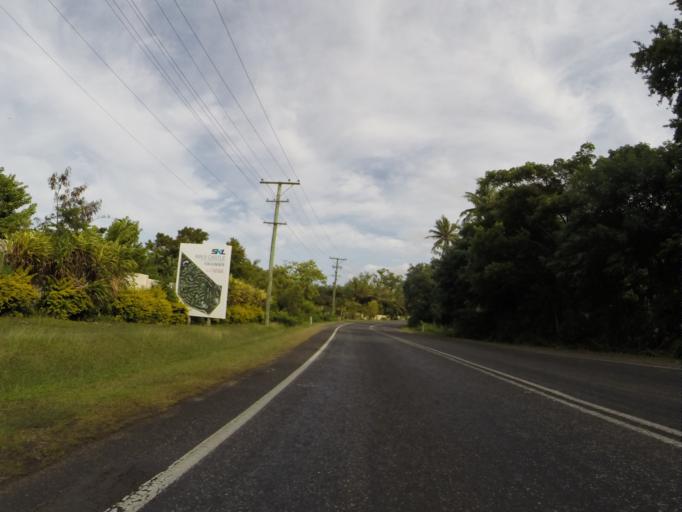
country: FJ
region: Western
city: Nadi
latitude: -18.2010
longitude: 177.6684
